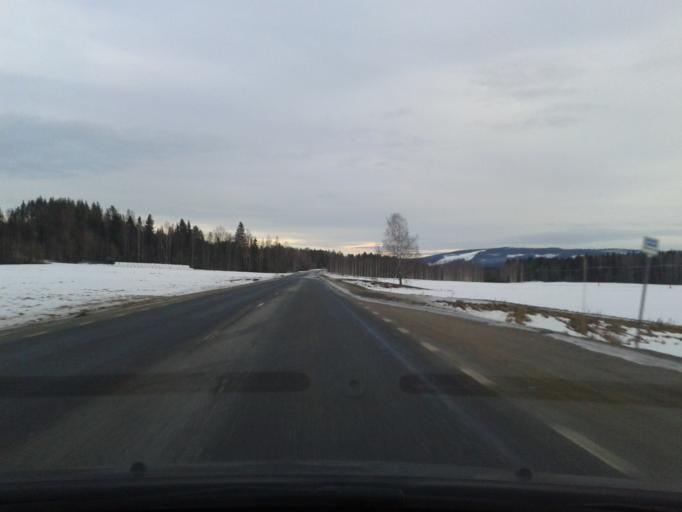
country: SE
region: Vaesternorrland
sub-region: Solleftea Kommun
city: Solleftea
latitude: 63.2271
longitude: 17.2177
